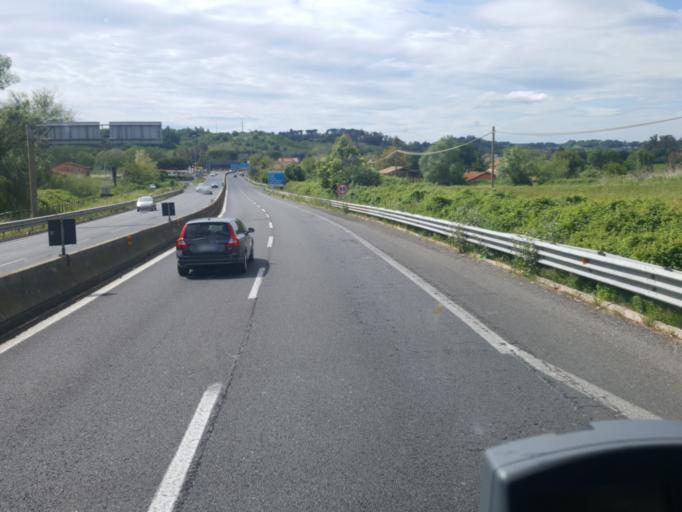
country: IT
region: Latium
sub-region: Citta metropolitana di Roma Capitale
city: Ara Nova
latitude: 41.9051
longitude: 12.2695
